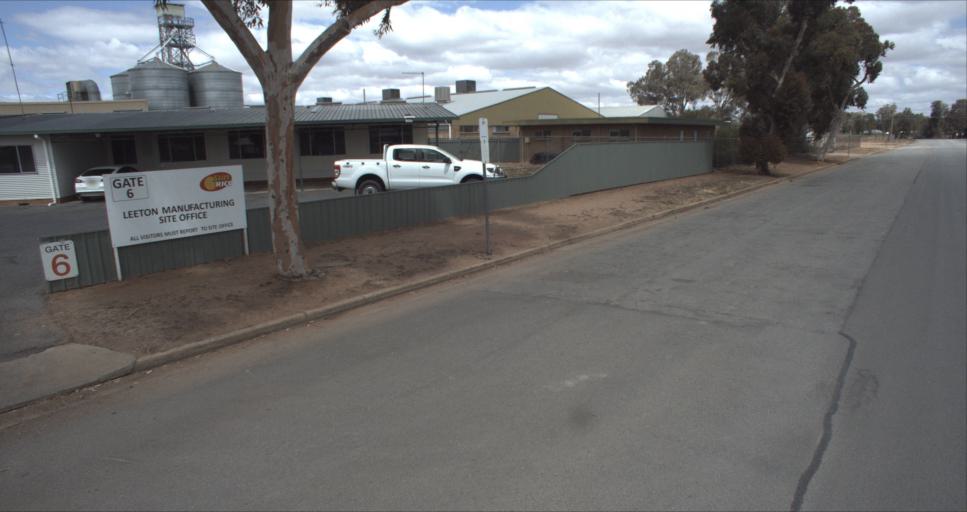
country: AU
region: New South Wales
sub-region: Leeton
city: Leeton
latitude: -34.5568
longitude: 146.3926
